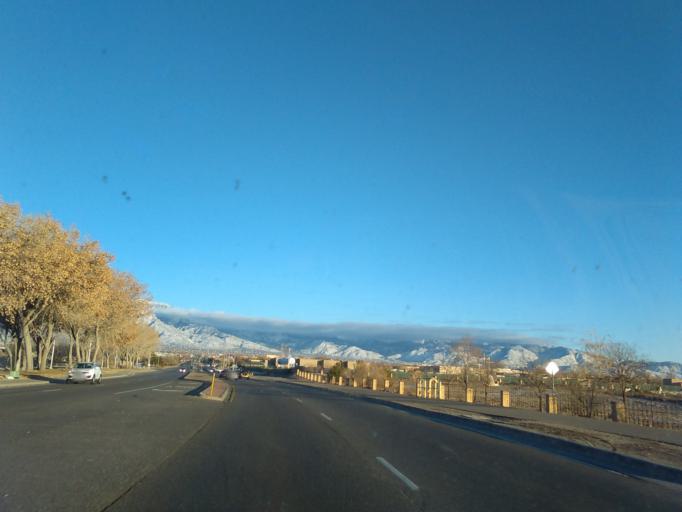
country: US
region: New Mexico
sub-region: Bernalillo County
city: North Valley
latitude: 35.1846
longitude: -106.6038
